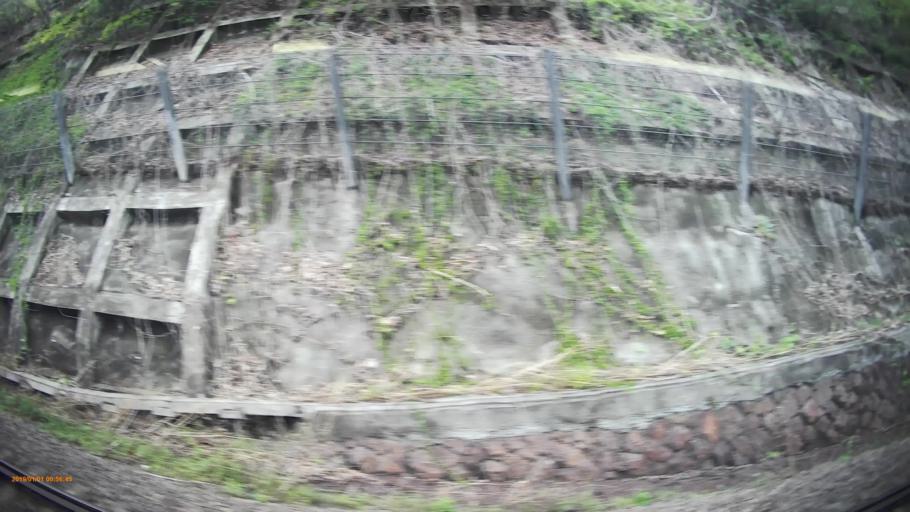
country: JP
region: Yamanashi
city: Otsuki
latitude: 35.6054
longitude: 138.8319
